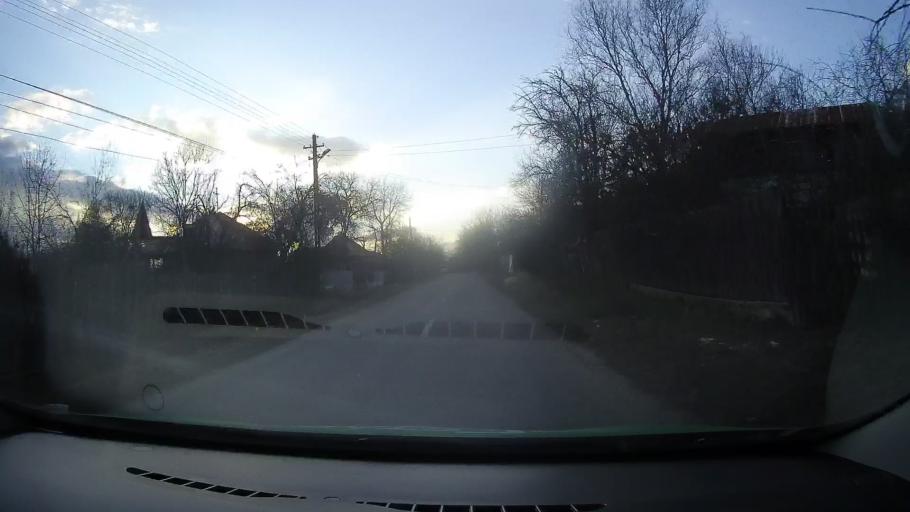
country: RO
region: Dambovita
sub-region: Comuna Gura Ocnitei
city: Adanca
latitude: 44.9358
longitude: 25.5927
